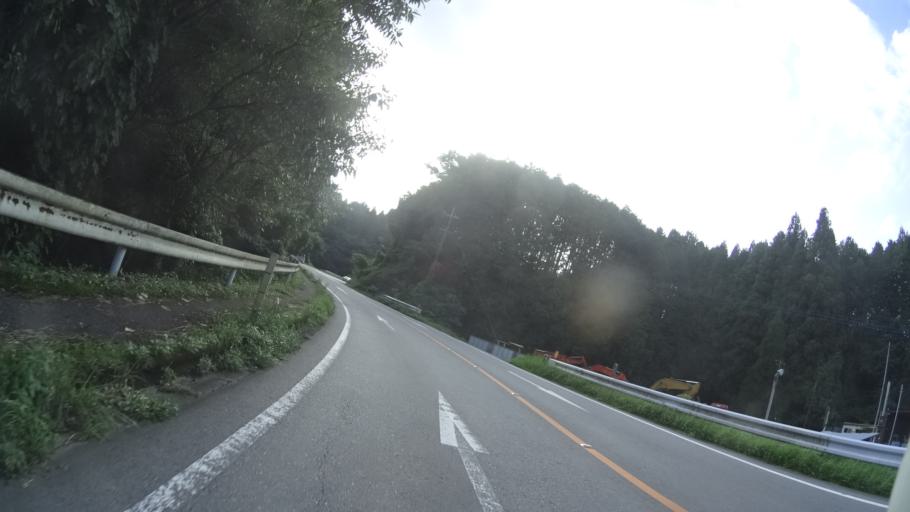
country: JP
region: Kumamoto
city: Ozu
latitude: 32.6865
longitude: 131.0057
